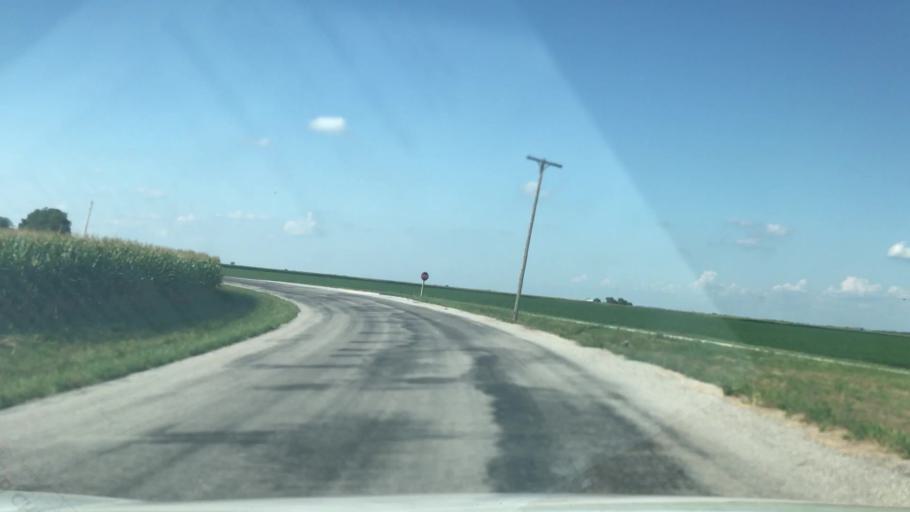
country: US
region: Illinois
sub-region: Washington County
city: Okawville
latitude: 38.4134
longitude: -89.4780
